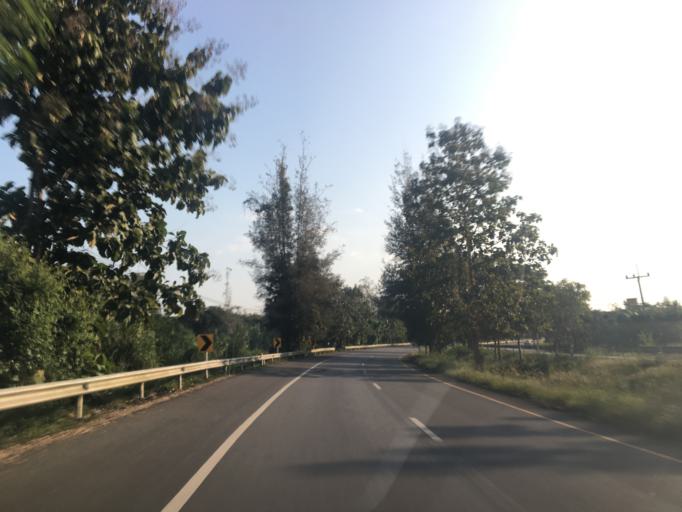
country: TH
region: Lampang
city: Ngao
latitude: 18.7640
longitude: 99.9737
